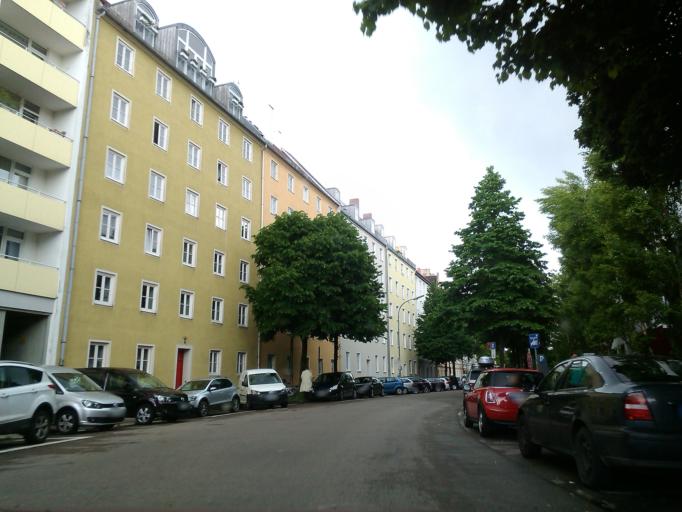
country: DE
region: Bavaria
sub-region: Upper Bavaria
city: Munich
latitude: 48.1276
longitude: 11.5906
